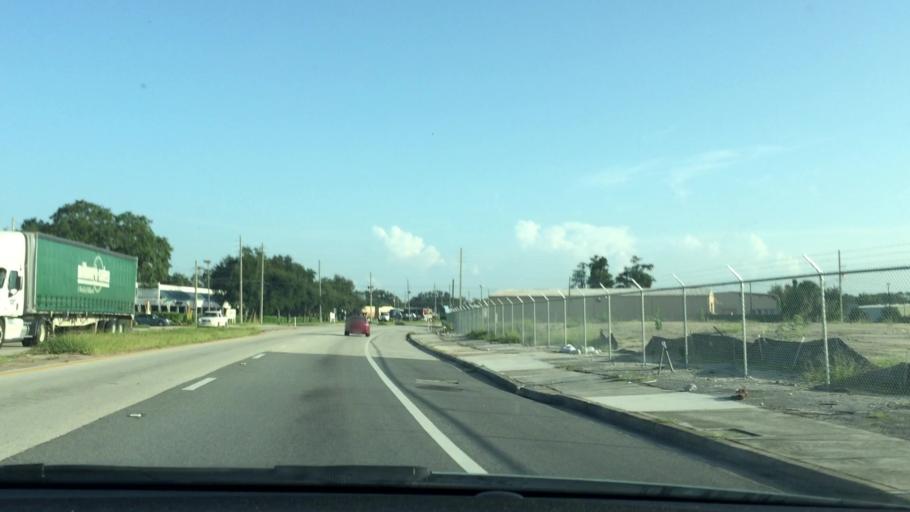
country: US
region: Florida
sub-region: Orange County
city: Fairview Shores
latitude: 28.5730
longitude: -81.4061
